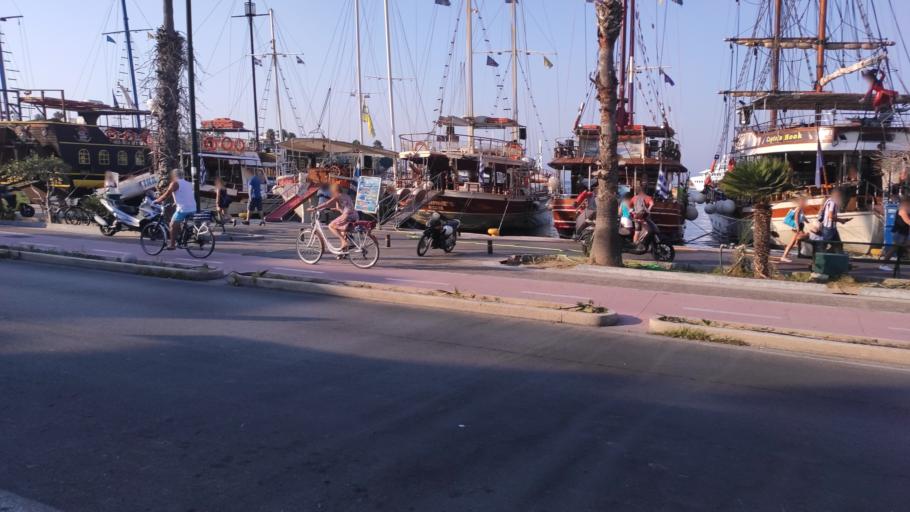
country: GR
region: South Aegean
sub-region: Nomos Dodekanisou
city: Kos
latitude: 36.8947
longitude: 27.2871
